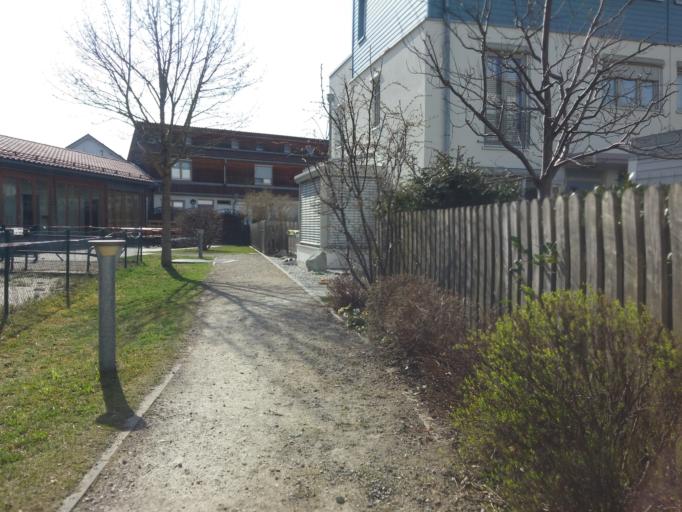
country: DE
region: Bavaria
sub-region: Upper Bavaria
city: Feldkirchen
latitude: 48.1312
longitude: 11.7159
